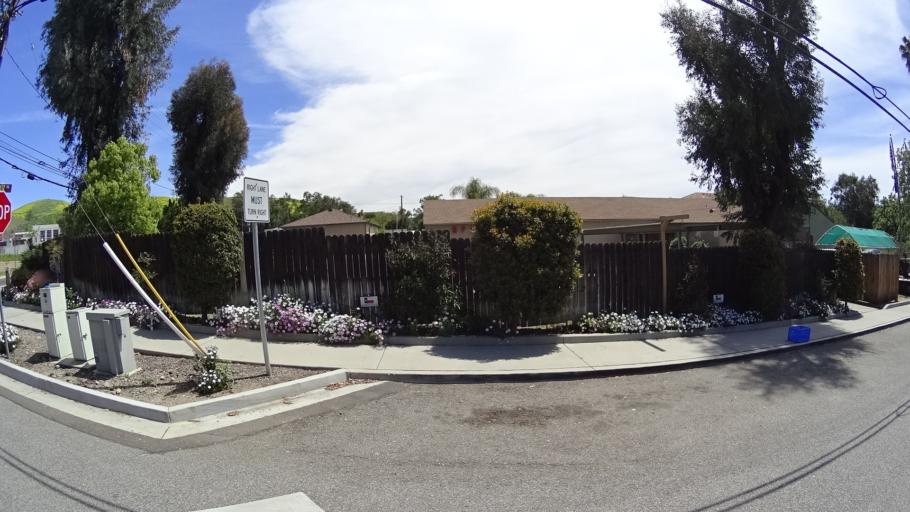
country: US
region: California
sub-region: Ventura County
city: Thousand Oaks
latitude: 34.1768
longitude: -118.8437
